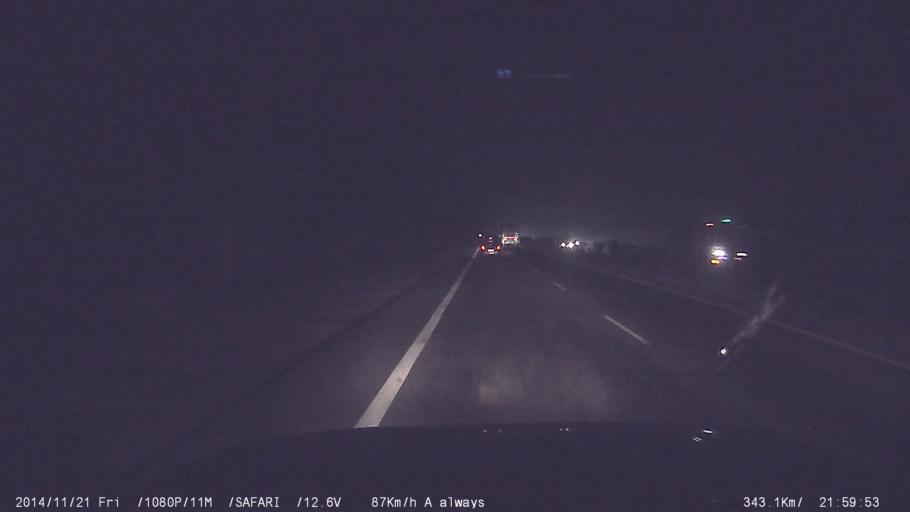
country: IN
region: Tamil Nadu
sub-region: Kancheepuram
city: Madurantakam
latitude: 12.5698
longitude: 79.9157
